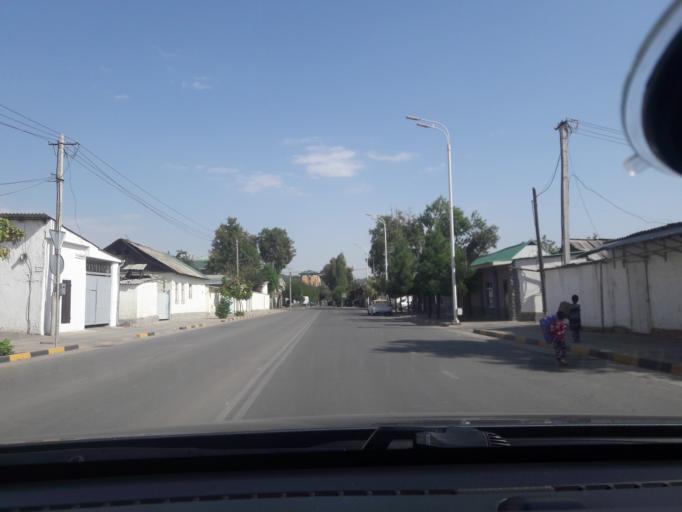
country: TJ
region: Dushanbe
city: Dushanbe
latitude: 38.5656
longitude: 68.8034
